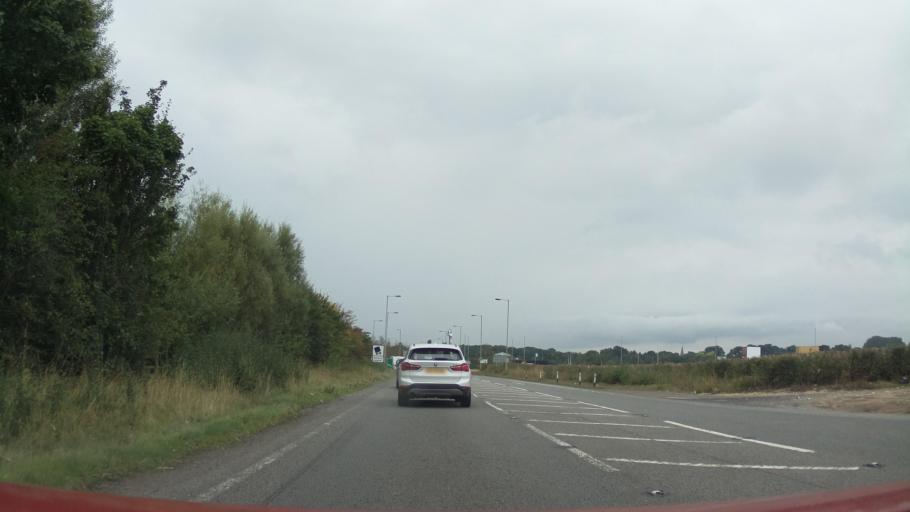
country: GB
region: England
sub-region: Nottinghamshire
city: South Collingham
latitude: 53.0942
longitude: -0.7765
